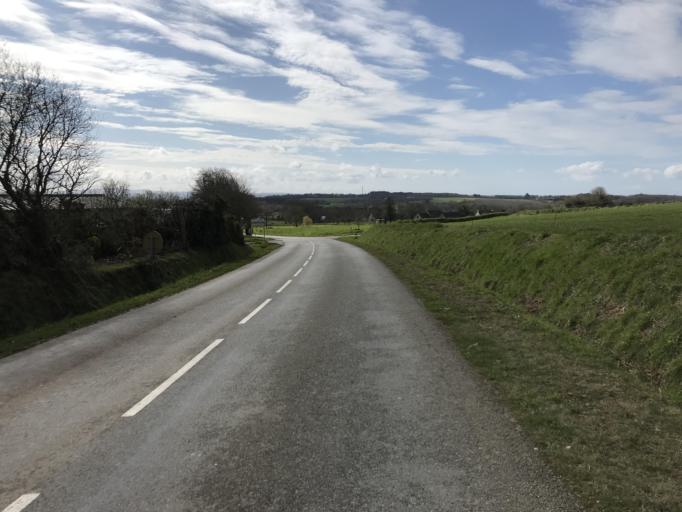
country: FR
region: Brittany
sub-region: Departement du Finistere
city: Dirinon
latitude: 48.3917
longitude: -4.2665
